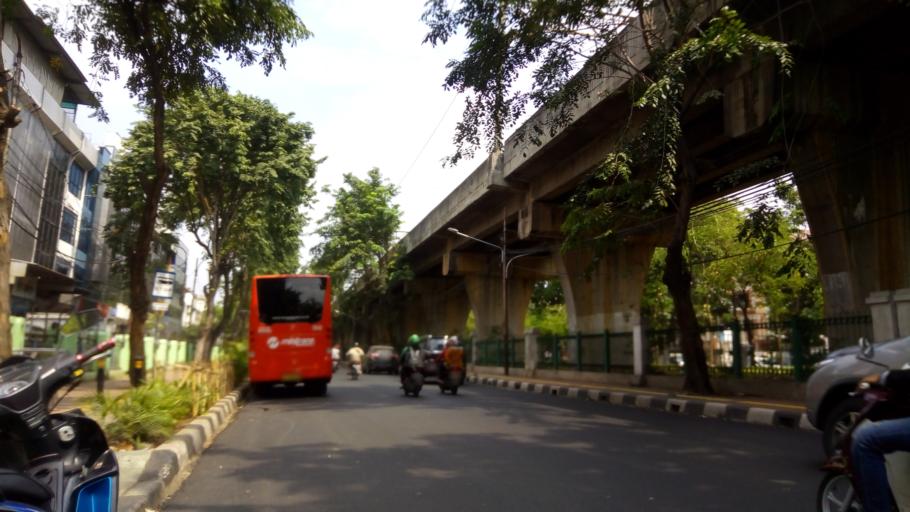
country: ID
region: Jakarta Raya
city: Jakarta
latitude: -6.1532
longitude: 106.8278
